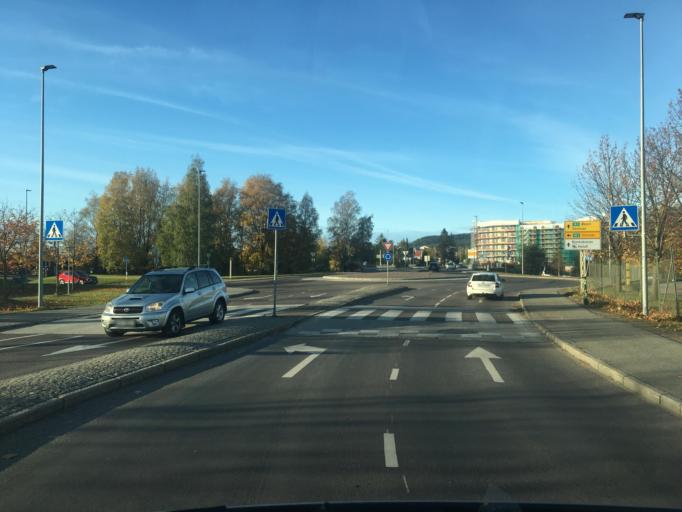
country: NO
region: Oslo
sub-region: Oslo
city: Oslo
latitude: 59.9319
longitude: 10.8297
